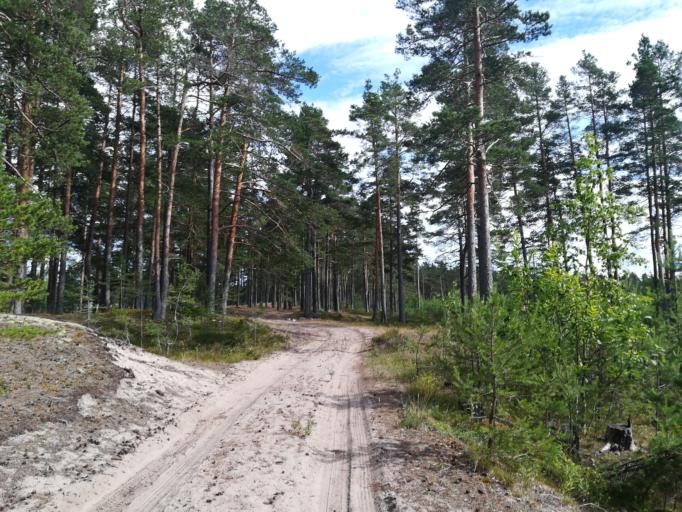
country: RU
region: Leningrad
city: Ust'-Luga
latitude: 59.6819
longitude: 28.2285
